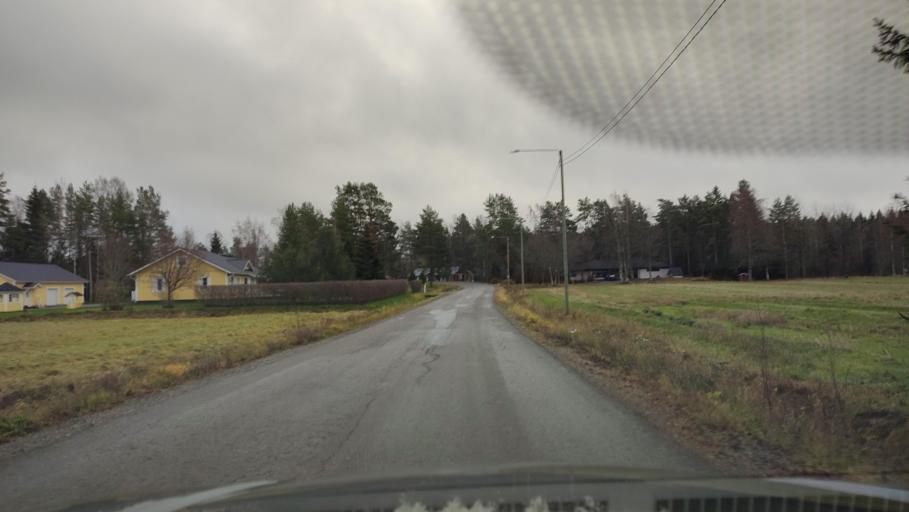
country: FI
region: Southern Ostrobothnia
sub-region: Suupohja
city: Karijoki
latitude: 62.1464
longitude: 21.5610
